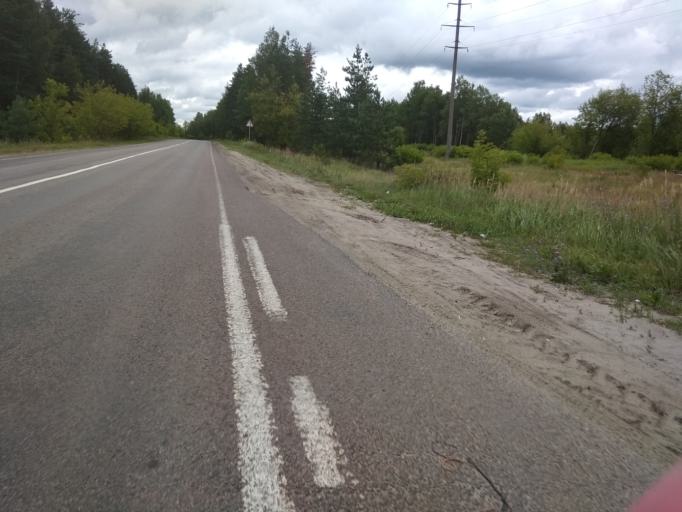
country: RU
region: Moskovskaya
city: Kerva
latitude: 55.5795
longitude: 39.6895
